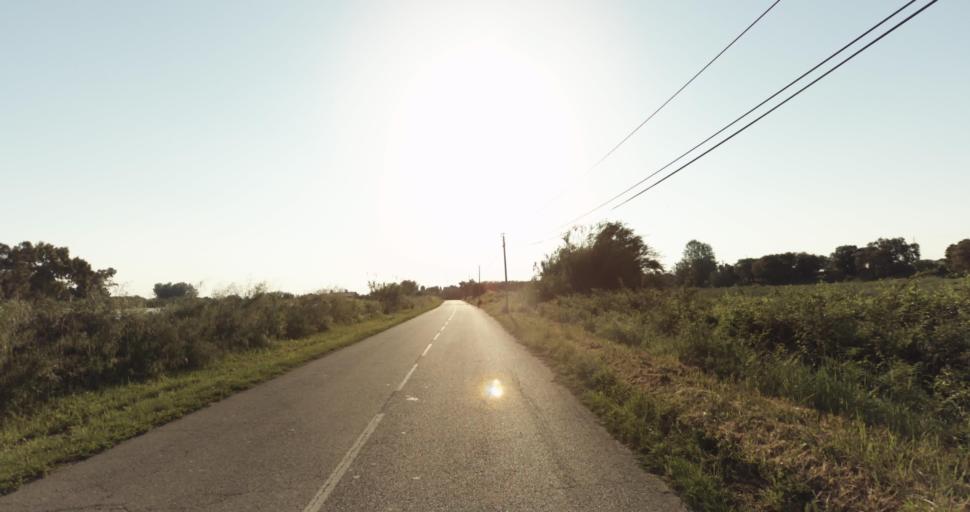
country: FR
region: Corsica
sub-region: Departement de la Haute-Corse
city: Biguglia
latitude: 42.6107
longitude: 9.4400
